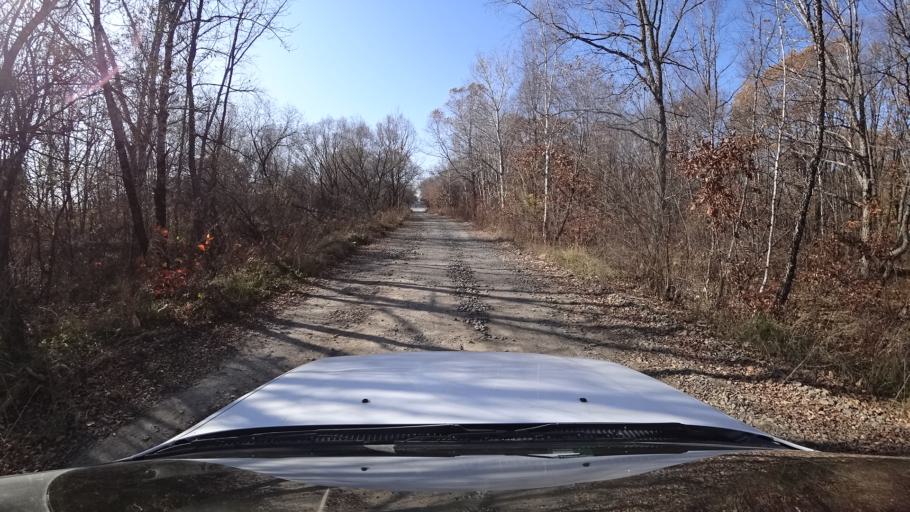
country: RU
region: Primorskiy
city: Dal'nerechensk
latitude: 45.8818
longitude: 133.7324
